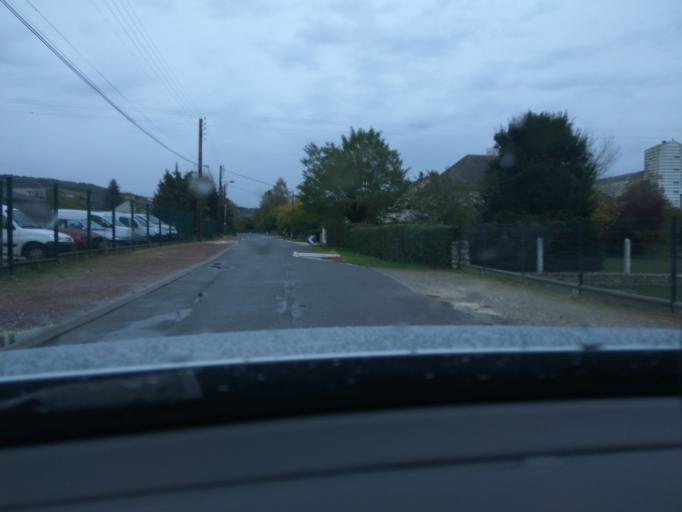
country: FR
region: Centre
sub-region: Departement du Cher
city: Saint-Satur
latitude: 47.3356
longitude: 2.8563
